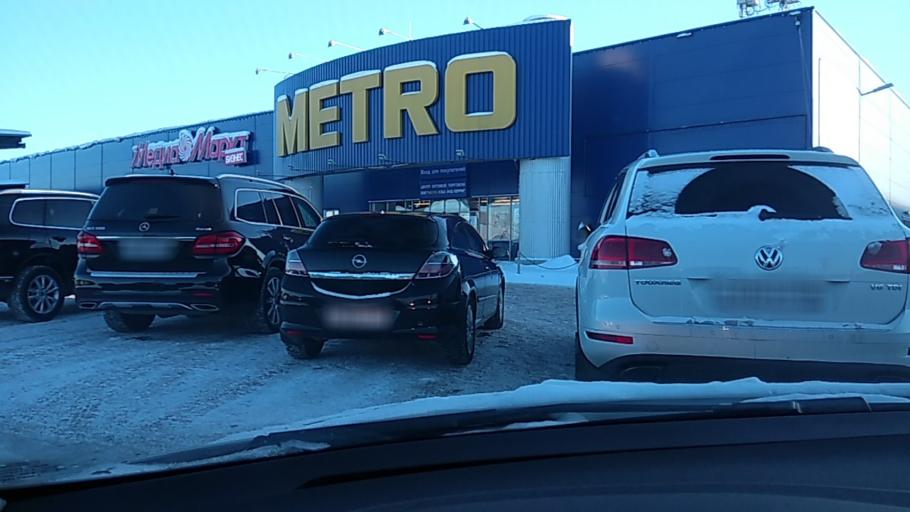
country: RU
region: Sverdlovsk
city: Shirokaya Rechka
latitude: 56.8249
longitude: 60.5099
